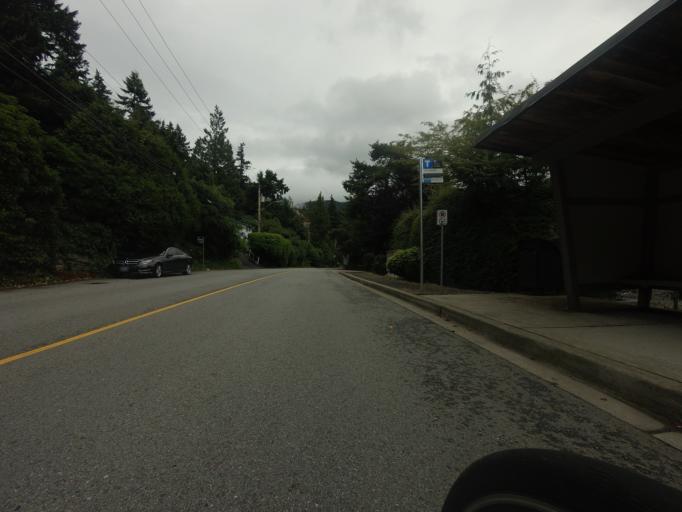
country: CA
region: British Columbia
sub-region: Greater Vancouver Regional District
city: Bowen Island
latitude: 49.3572
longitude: -123.2732
